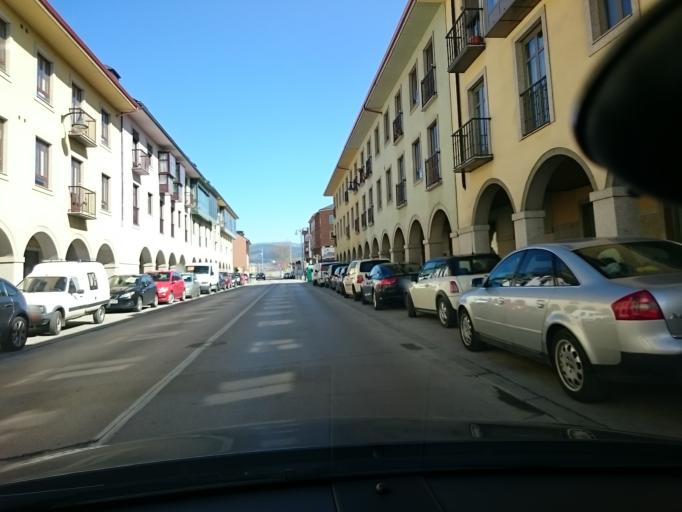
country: ES
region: Castille and Leon
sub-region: Provincia de Leon
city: Ponferrada
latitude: 42.5428
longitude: -6.5915
